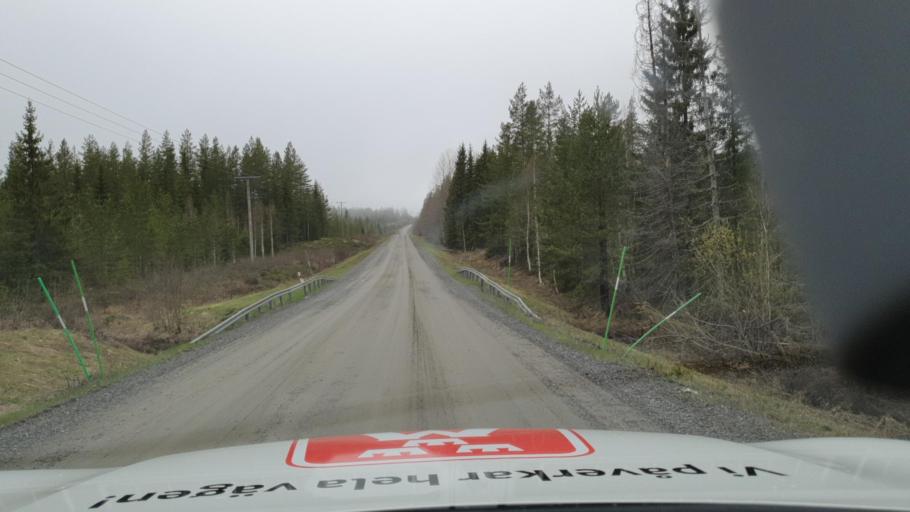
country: SE
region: Vaesterbotten
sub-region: Nordmalings Kommun
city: Nordmaling
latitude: 63.7660
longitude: 19.4742
